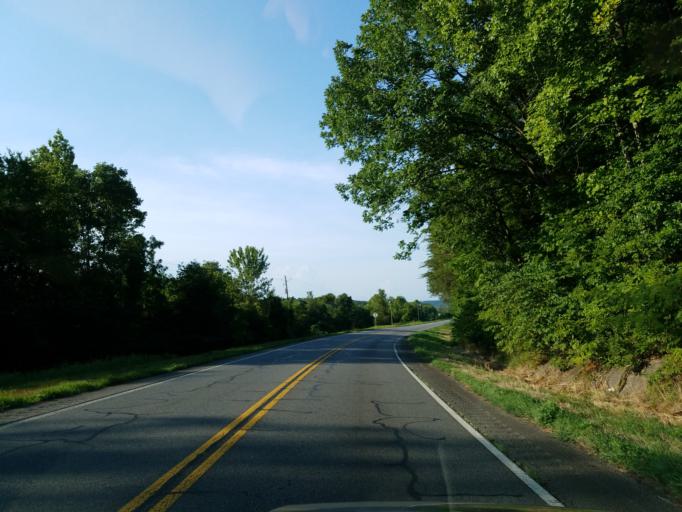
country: US
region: Georgia
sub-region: Bartow County
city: Rydal
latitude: 34.3994
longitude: -84.7091
